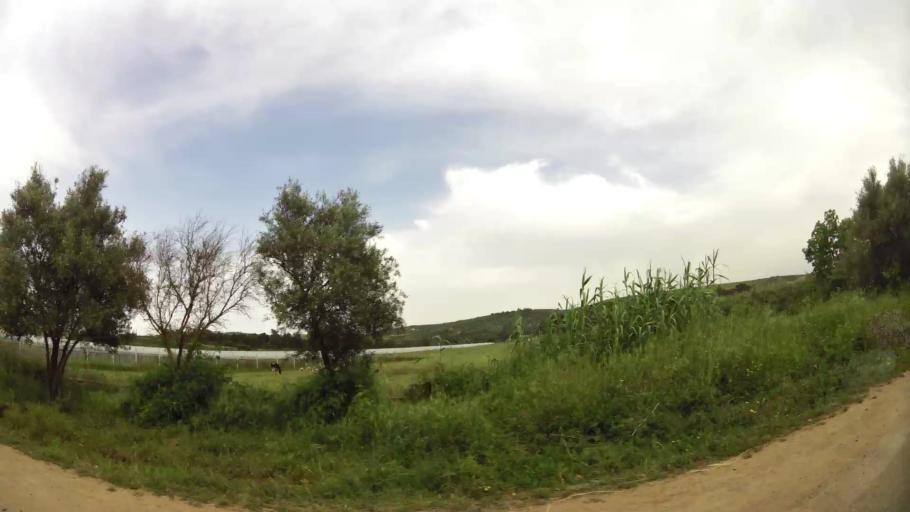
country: MA
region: Rabat-Sale-Zemmour-Zaer
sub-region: Khemisset
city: Khemisset
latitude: 33.7486
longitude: -6.2025
